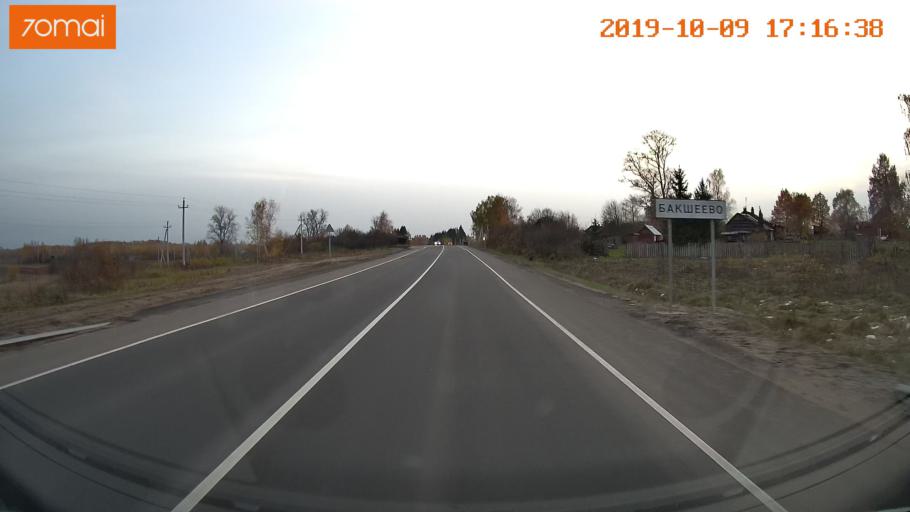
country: RU
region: Ivanovo
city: Furmanov
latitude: 57.2860
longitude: 41.1626
